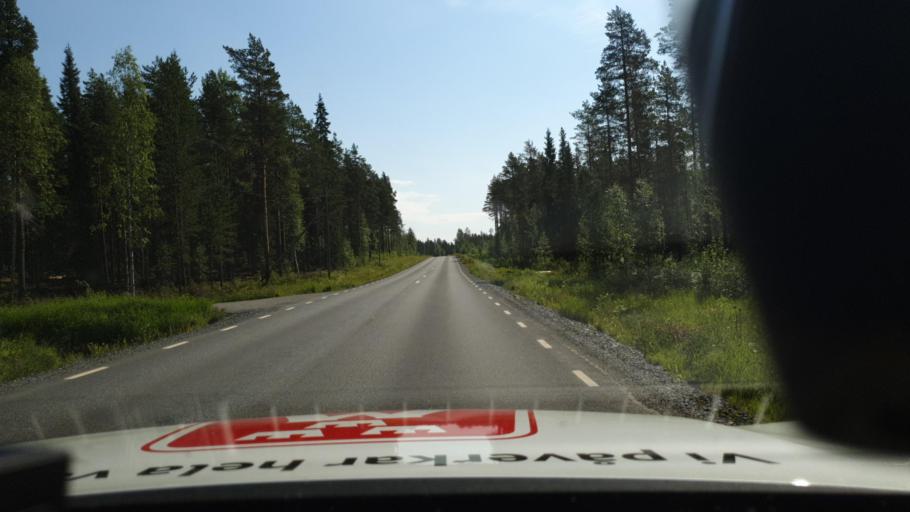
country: SE
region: Norrbotten
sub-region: Lulea Kommun
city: Ranea
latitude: 65.7906
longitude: 22.1320
